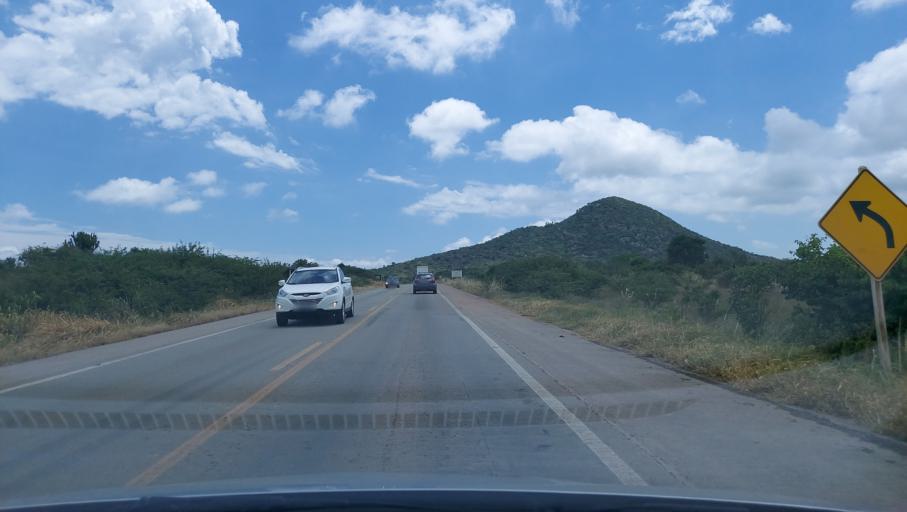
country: BR
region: Bahia
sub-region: Seabra
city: Seabra
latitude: -12.4283
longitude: -42.0022
